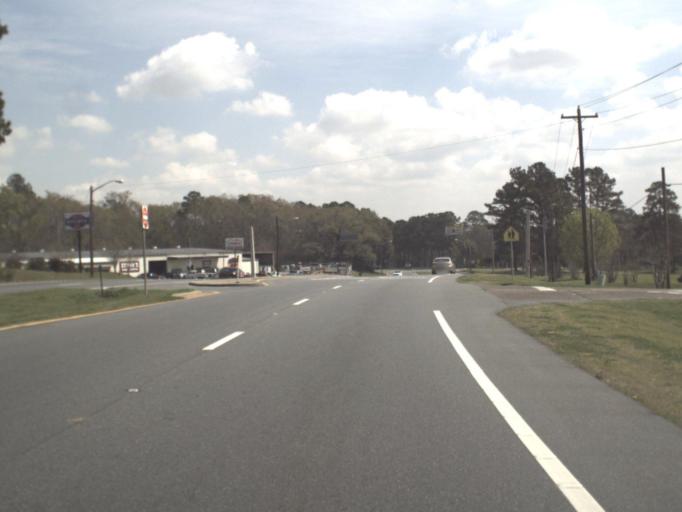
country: US
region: Florida
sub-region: Gadsden County
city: Havana
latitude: 30.6153
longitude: -84.4204
